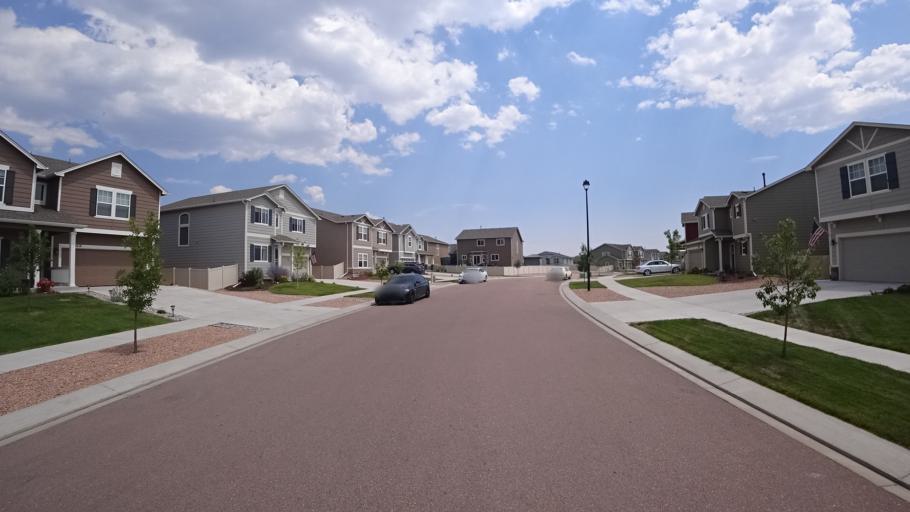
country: US
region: Colorado
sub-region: El Paso County
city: Black Forest
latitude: 38.9544
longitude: -104.6983
